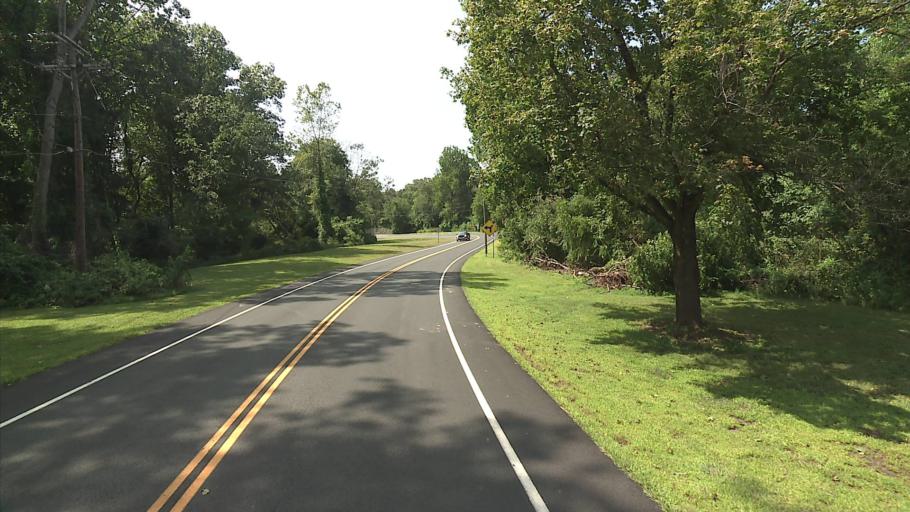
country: US
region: Connecticut
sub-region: Hartford County
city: Broad Brook
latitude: 41.9138
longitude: -72.5542
